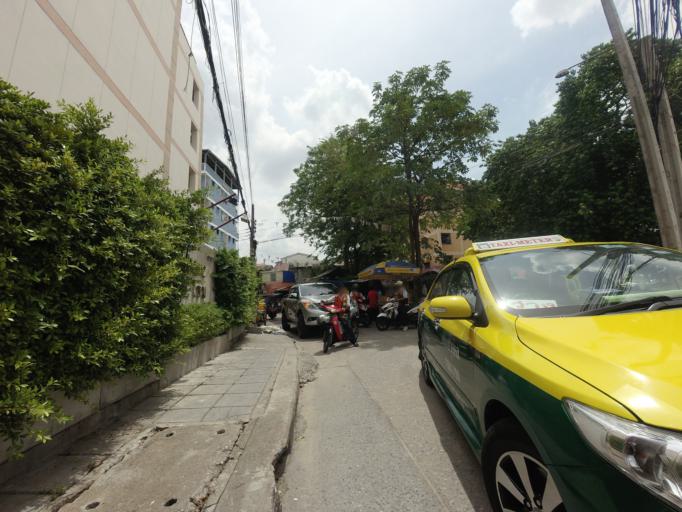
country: TH
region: Bangkok
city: Din Daeng
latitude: 13.7747
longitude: 100.5569
